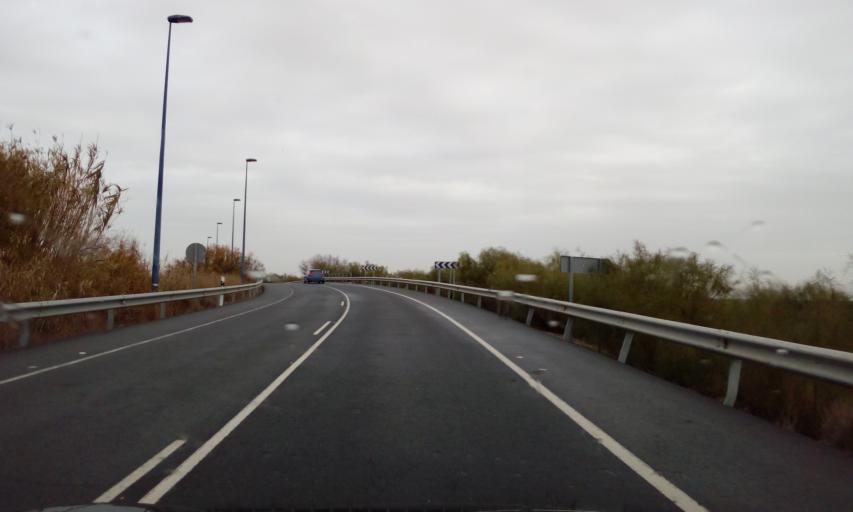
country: ES
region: Andalusia
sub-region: Provincia de Huelva
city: Lepe
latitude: 37.2124
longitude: -7.1956
